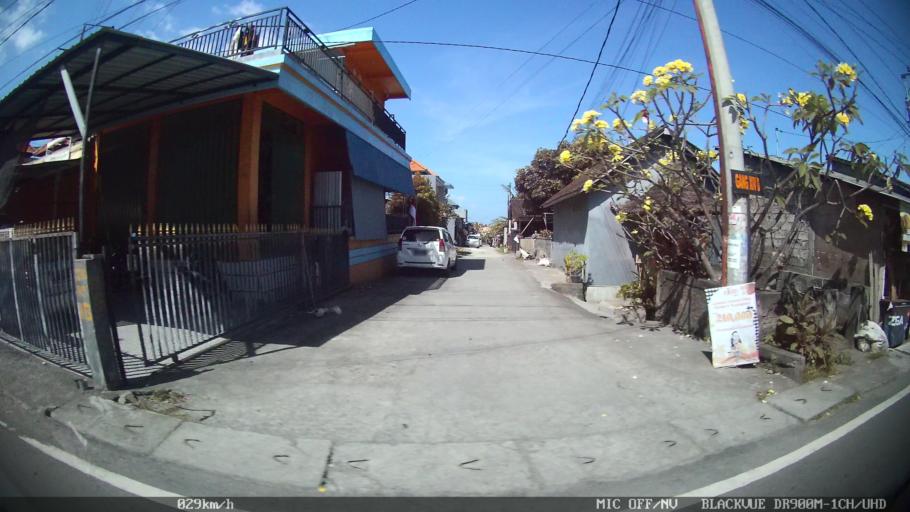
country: ID
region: Bali
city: Denpasar
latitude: -8.6538
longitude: 115.1808
